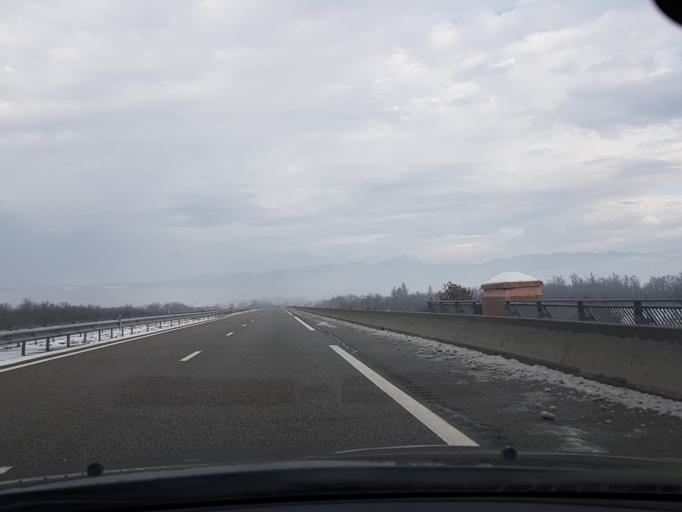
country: FR
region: Provence-Alpes-Cote d'Azur
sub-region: Departement des Alpes-de-Haute-Provence
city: Sisteron
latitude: 44.2650
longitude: 5.9060
